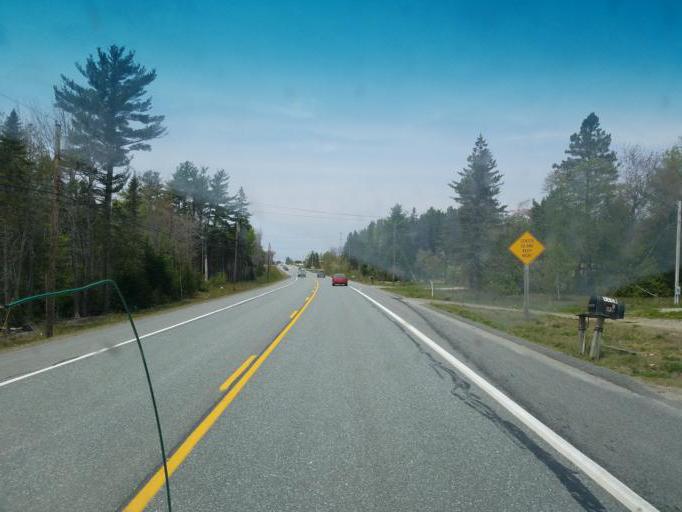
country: US
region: Maine
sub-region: Hancock County
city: Surry
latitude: 44.6119
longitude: -68.5216
